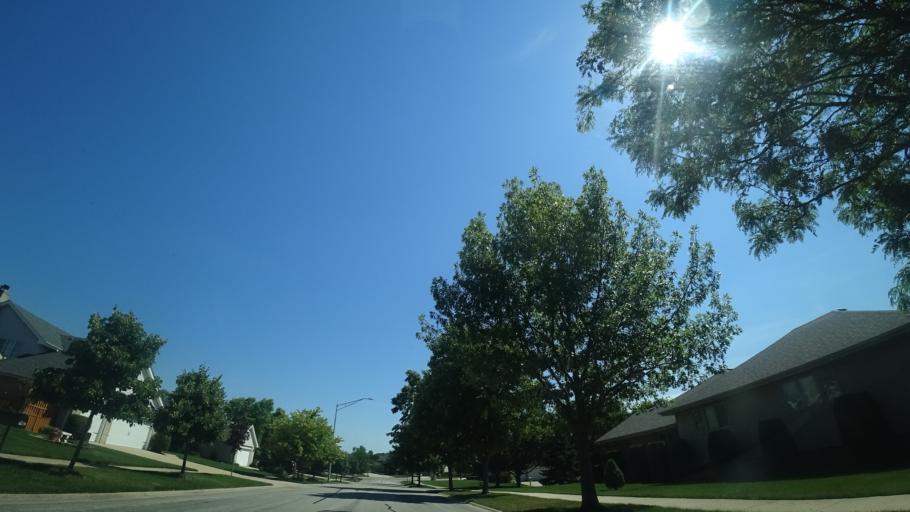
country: US
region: Illinois
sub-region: Will County
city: Mokena
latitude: 41.5631
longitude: -87.8947
